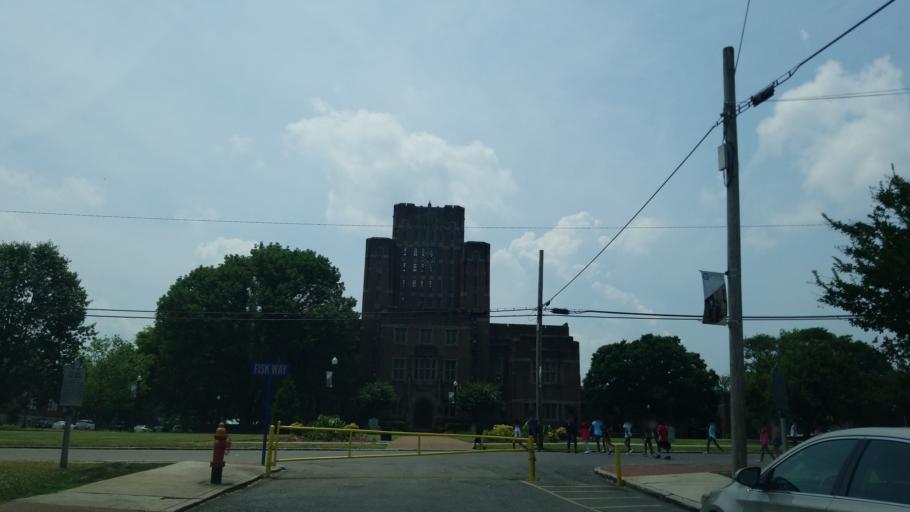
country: US
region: Tennessee
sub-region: Davidson County
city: Nashville
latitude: 36.1675
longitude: -86.8037
